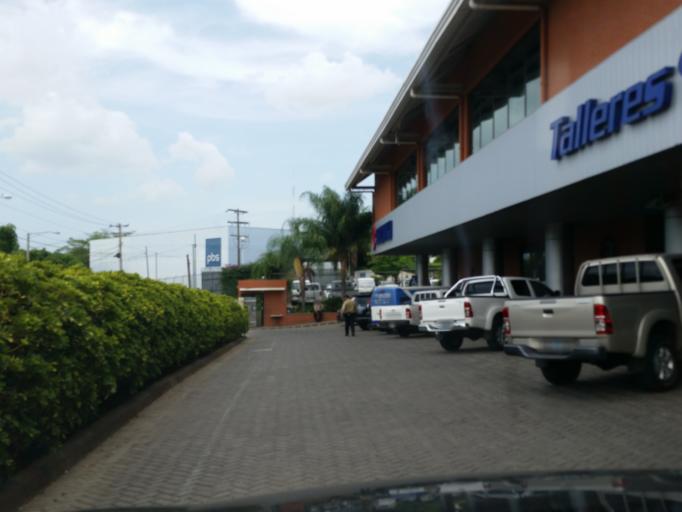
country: NI
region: Managua
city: Managua
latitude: 12.1315
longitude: -86.2825
